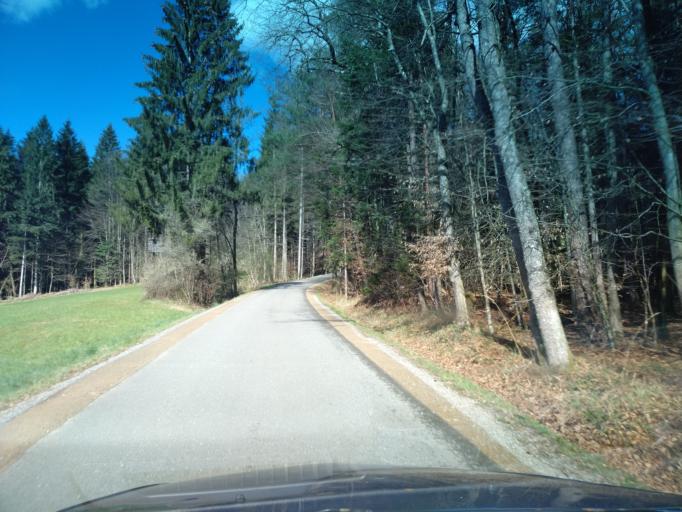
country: AT
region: Styria
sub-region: Politischer Bezirk Leibnitz
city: Sankt Johann im Saggautal
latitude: 46.7135
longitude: 15.3895
